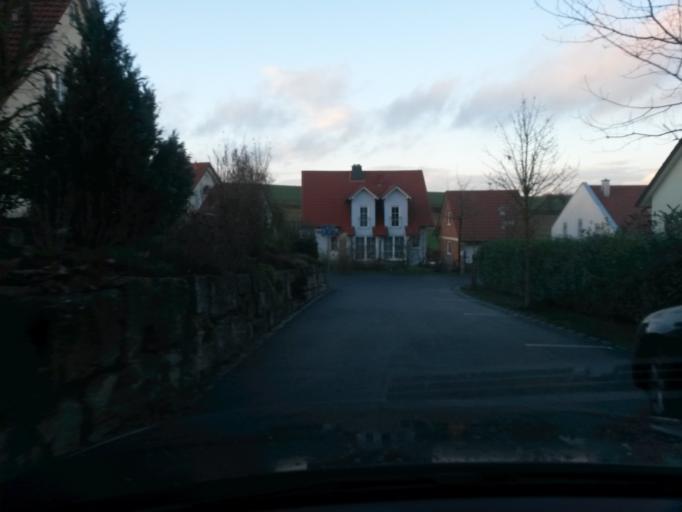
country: DE
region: Bavaria
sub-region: Regierungsbezirk Unterfranken
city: Estenfeld
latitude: 49.8322
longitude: 10.0043
